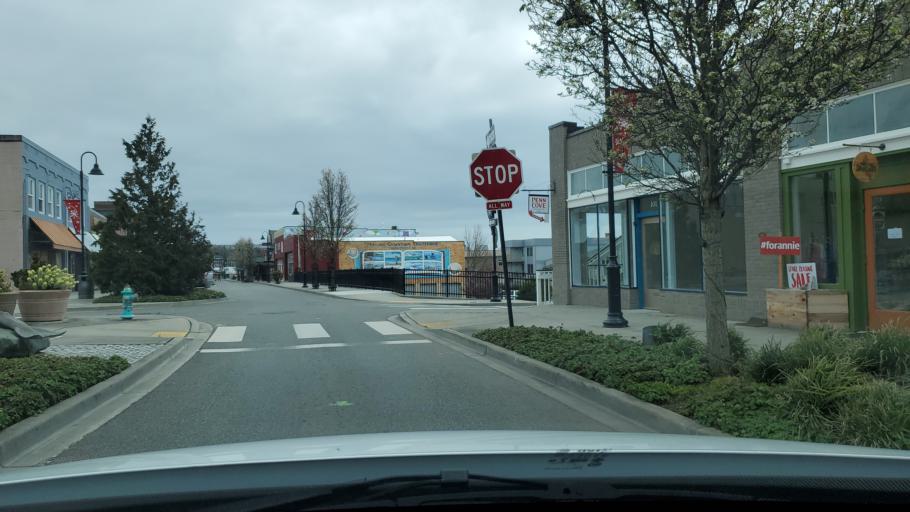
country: US
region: Washington
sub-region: Island County
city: Oak Harbor
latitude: 48.2882
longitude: -122.6487
